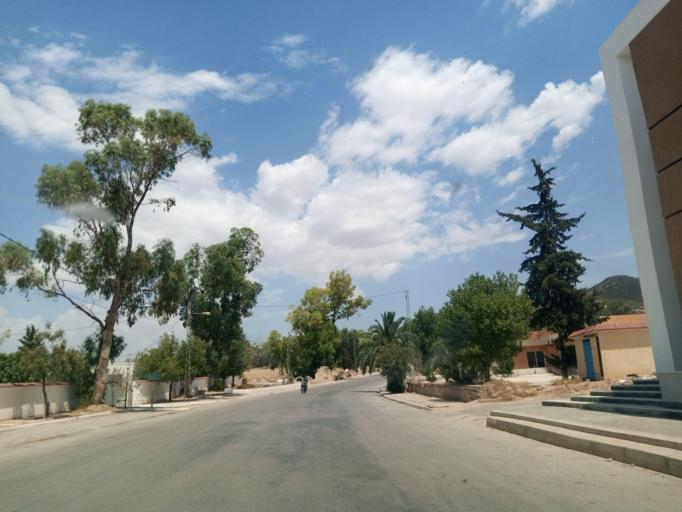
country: TN
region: Kef
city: Nibbar
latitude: 36.3068
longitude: 8.7727
